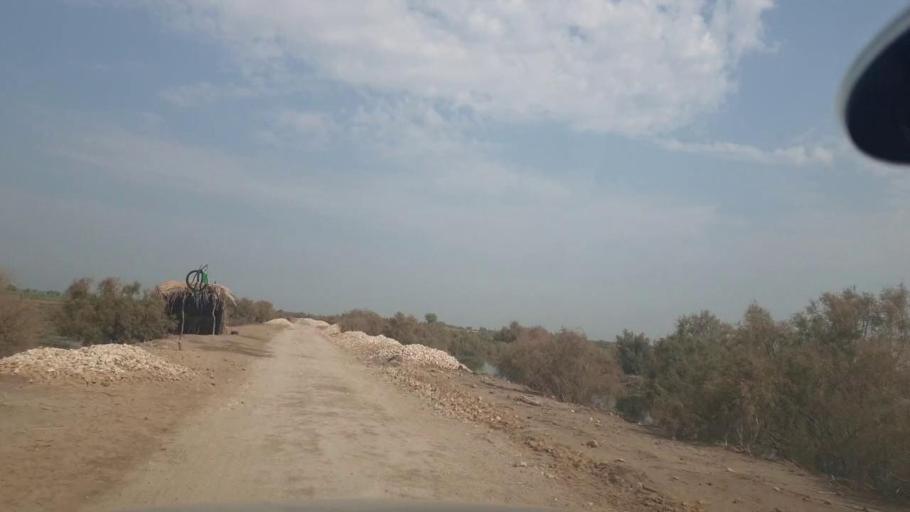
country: PK
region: Balochistan
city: Mehrabpur
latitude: 28.0898
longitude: 68.0966
